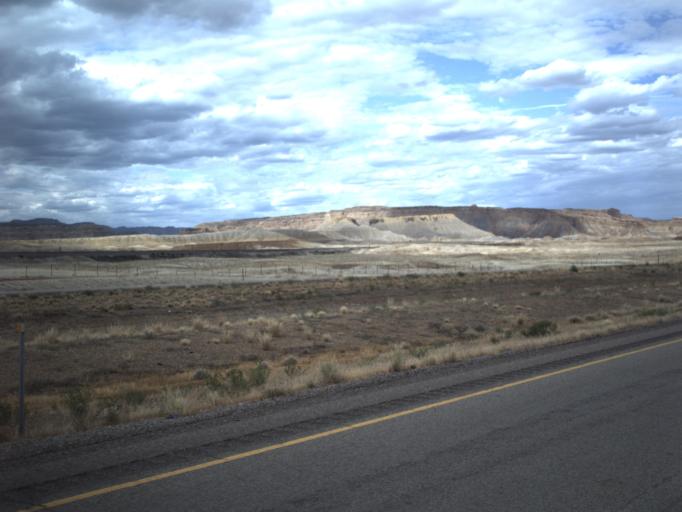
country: US
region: Utah
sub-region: Grand County
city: Moab
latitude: 38.9230
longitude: -109.9220
